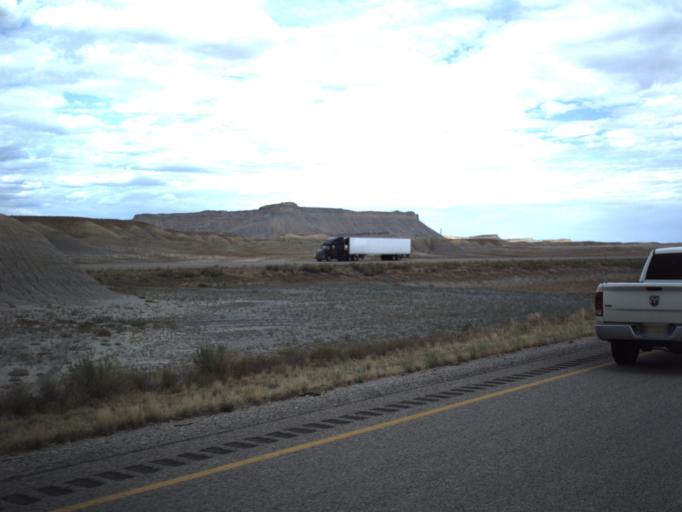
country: US
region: Utah
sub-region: Grand County
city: Moab
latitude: 38.9326
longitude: -110.0184
